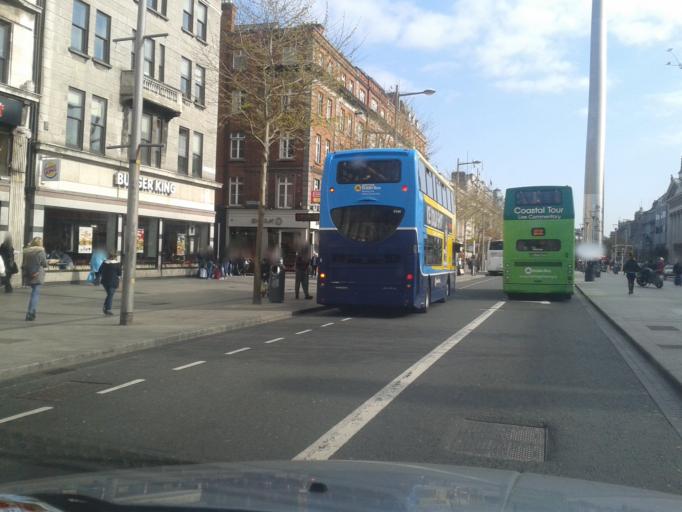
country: IE
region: Leinster
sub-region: Dublin City
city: Dublin
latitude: 53.3507
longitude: -6.2606
